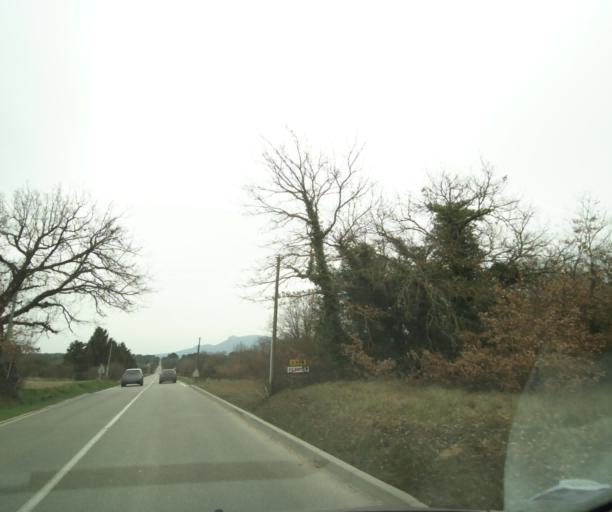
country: FR
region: Provence-Alpes-Cote d'Azur
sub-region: Departement des Bouches-du-Rhone
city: Peynier
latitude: 43.4461
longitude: 5.6481
